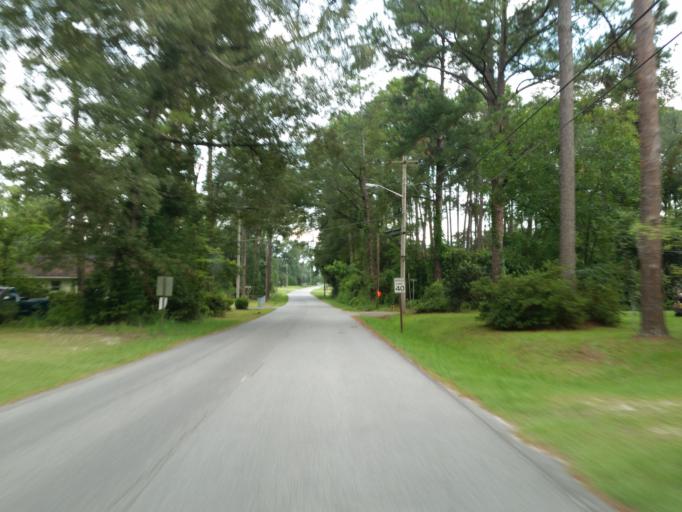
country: US
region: Georgia
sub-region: Cook County
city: Adel
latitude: 31.1270
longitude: -83.4169
